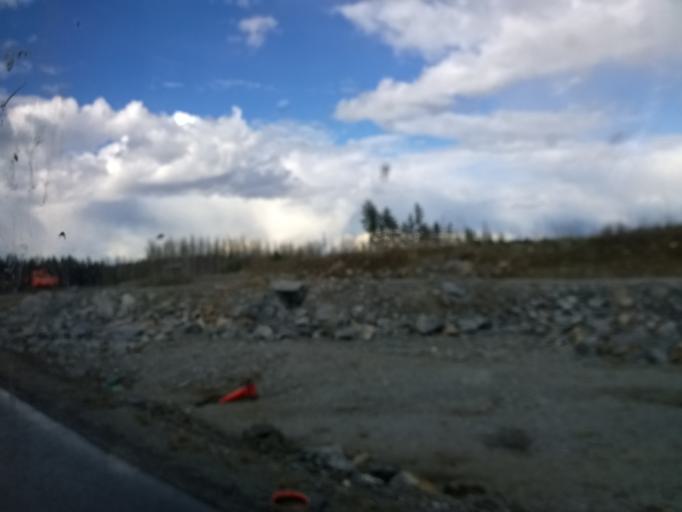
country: FI
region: Pirkanmaa
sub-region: Tampere
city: Tampere
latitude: 61.4581
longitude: 23.7912
